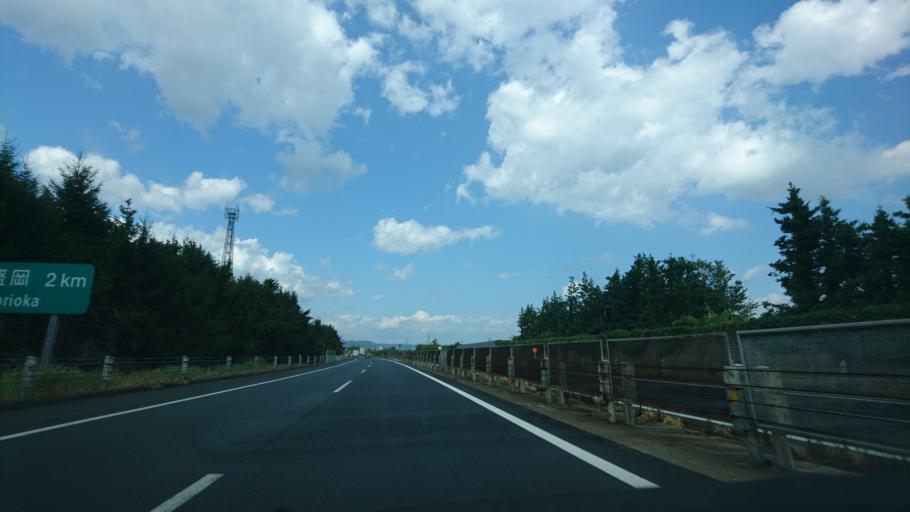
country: JP
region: Iwate
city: Morioka-shi
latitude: 39.6918
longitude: 141.1022
